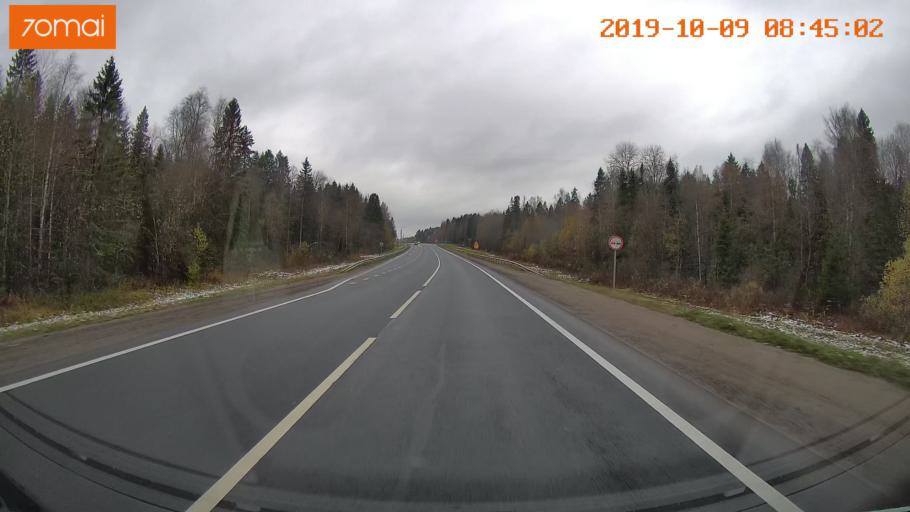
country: RU
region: Vologda
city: Gryazovets
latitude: 59.0440
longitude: 40.0993
